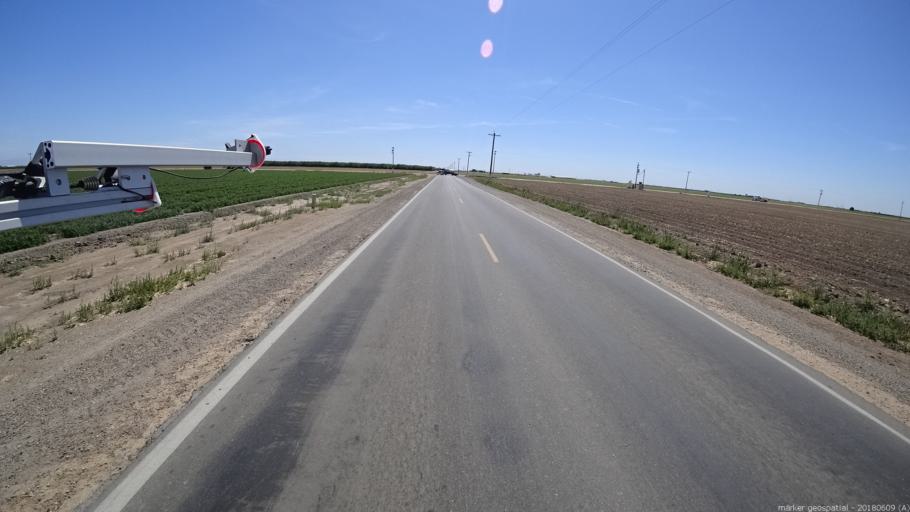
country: US
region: California
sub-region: Madera County
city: Fairmead
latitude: 36.9528
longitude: -120.2668
